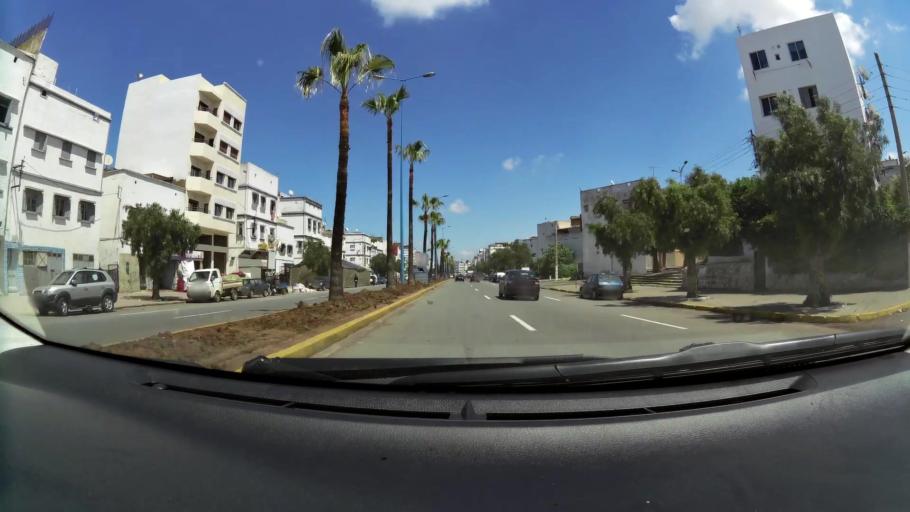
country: MA
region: Grand Casablanca
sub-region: Casablanca
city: Casablanca
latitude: 33.5610
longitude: -7.5738
